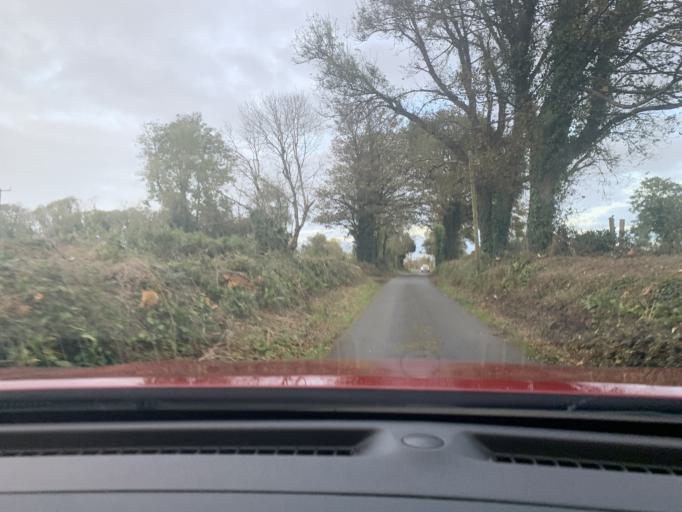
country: IE
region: Connaught
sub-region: Sligo
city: Tobercurry
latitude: 54.0913
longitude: -8.6743
